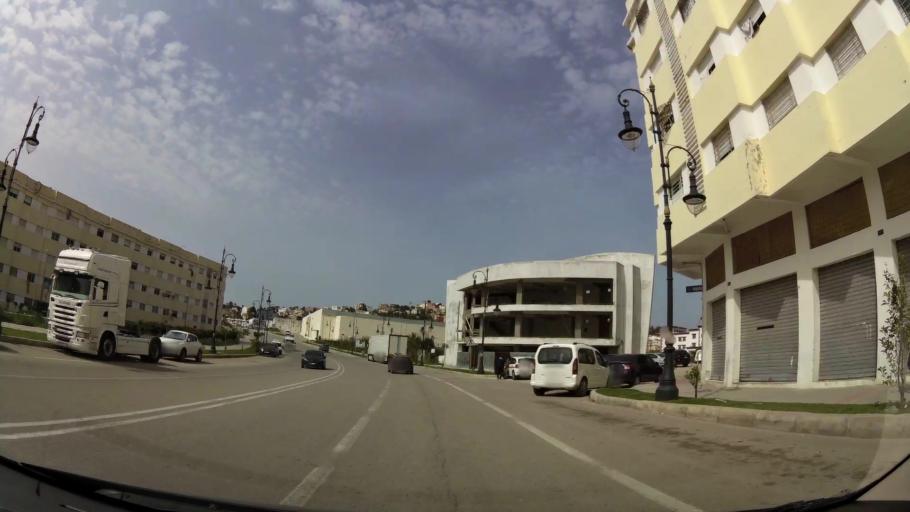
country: MA
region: Tanger-Tetouan
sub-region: Tanger-Assilah
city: Boukhalef
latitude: 35.7354
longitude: -5.8742
